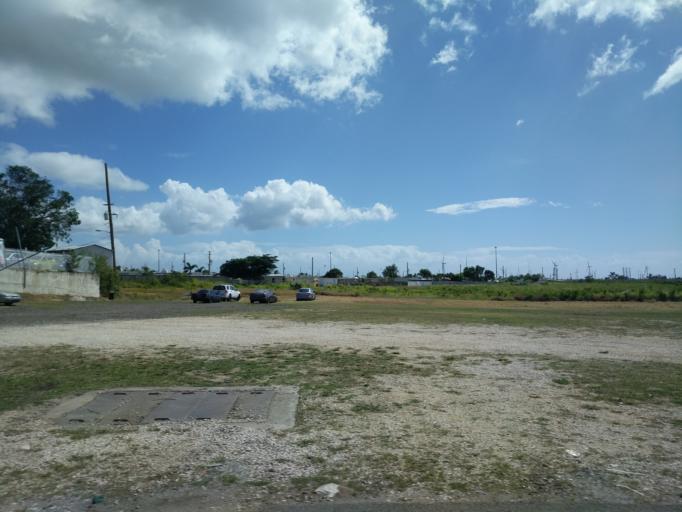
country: PR
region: Santa Isabel Municipio
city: El Ojo
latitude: 18.0150
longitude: -66.3799
